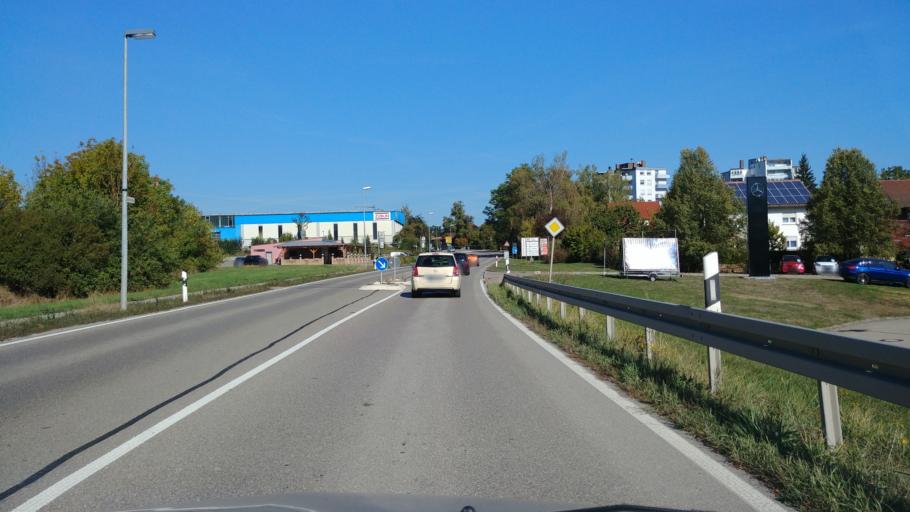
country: DE
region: Baden-Wuerttemberg
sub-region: Regierungsbezirk Stuttgart
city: Gaildorf
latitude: 48.9945
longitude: 9.7740
